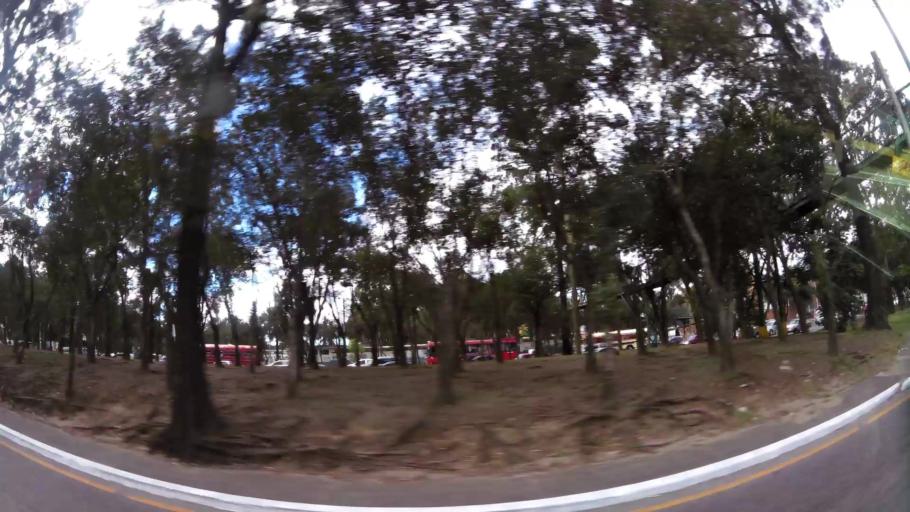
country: GT
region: Guatemala
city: Guatemala City
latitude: 14.6107
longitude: -90.5327
